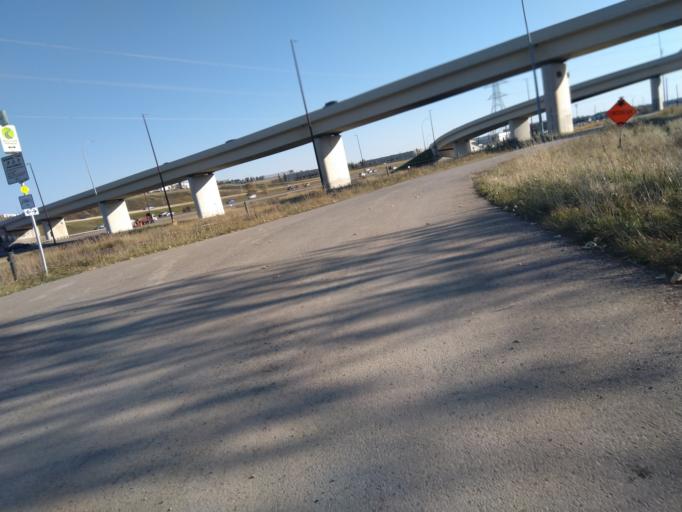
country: CA
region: Alberta
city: Calgary
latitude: 51.1265
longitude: -114.0482
